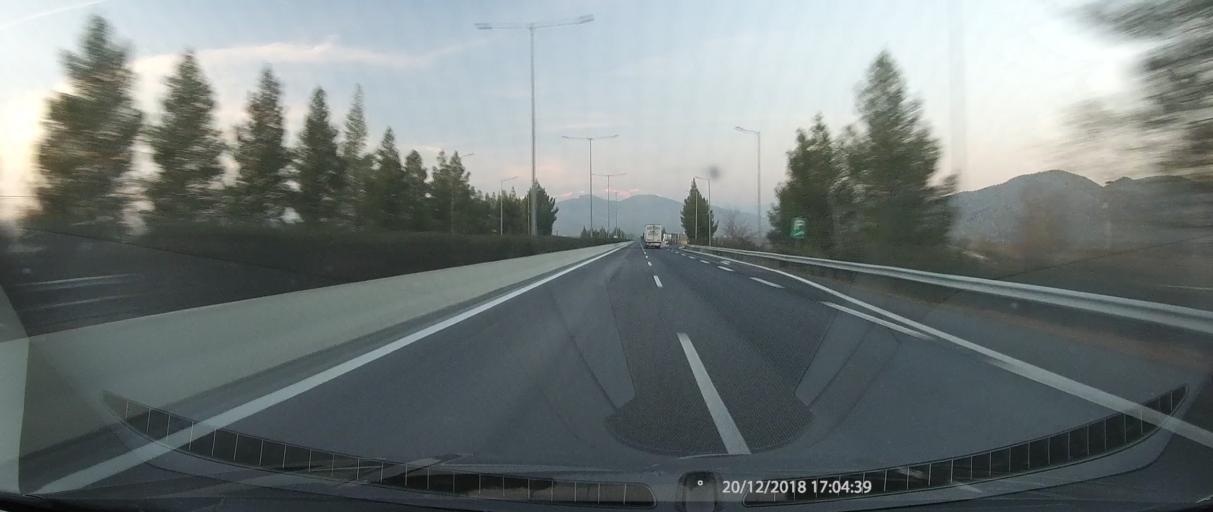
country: GR
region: Thessaly
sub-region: Nomos Larisis
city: Makrychori
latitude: 39.7221
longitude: 22.4810
